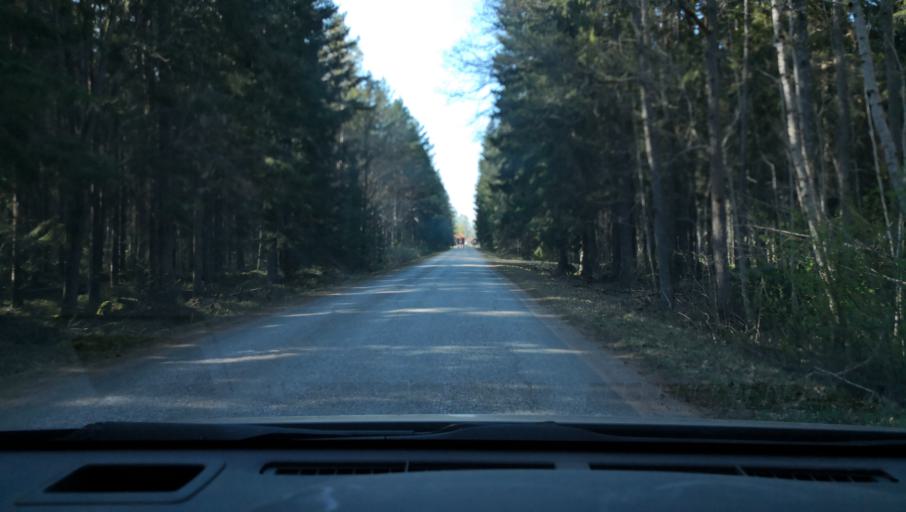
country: SE
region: Uppsala
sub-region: Heby Kommun
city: Tarnsjo
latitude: 60.2803
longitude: 16.8881
